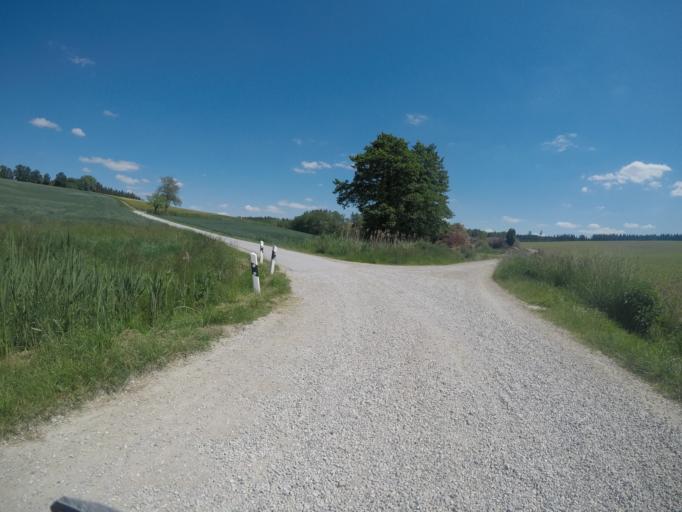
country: DE
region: Bavaria
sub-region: Lower Bavaria
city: Kumhausen
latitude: 48.4858
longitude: 12.1678
